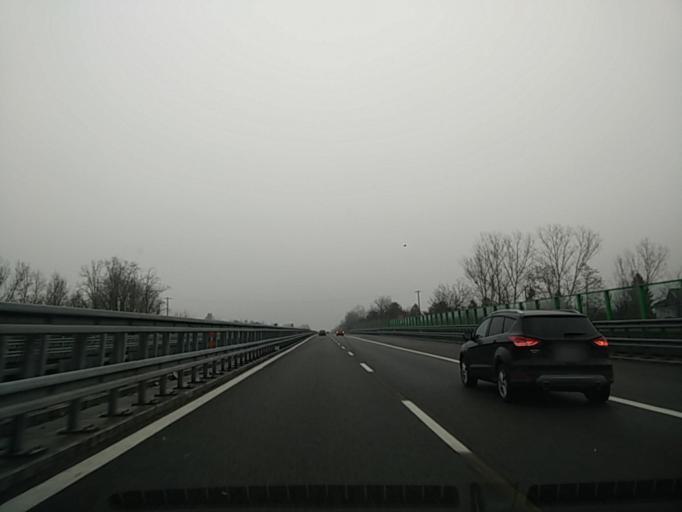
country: IT
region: Piedmont
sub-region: Provincia di Asti
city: Revigliasco d'Asti
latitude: 44.9030
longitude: 8.1467
